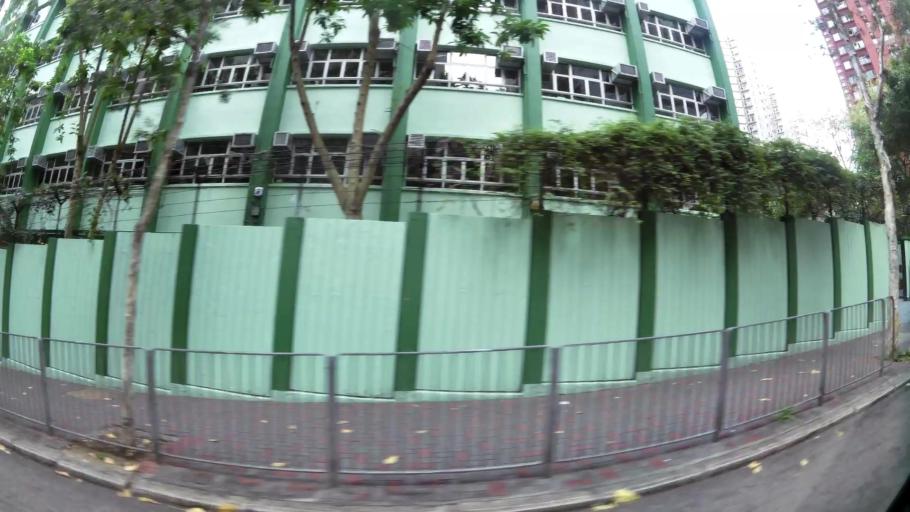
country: HK
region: Kowloon City
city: Kowloon
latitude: 22.3067
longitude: 114.2352
